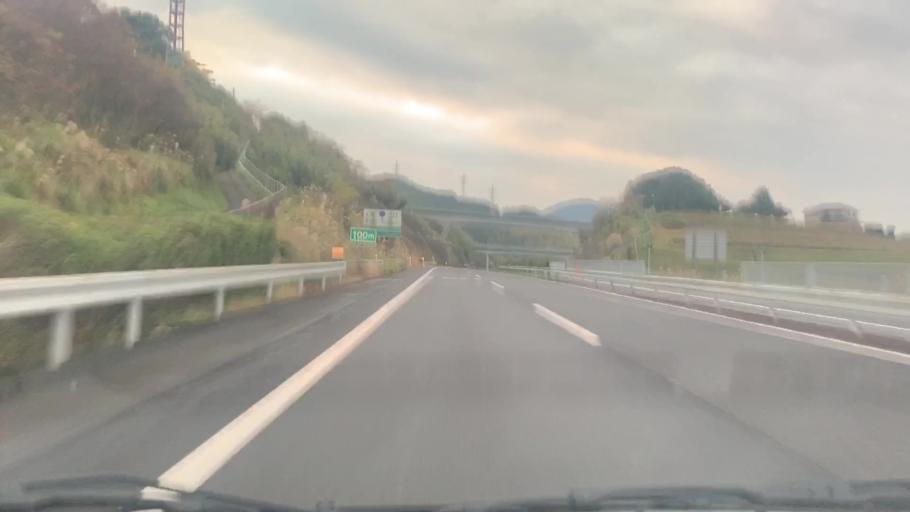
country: JP
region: Nagasaki
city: Omura
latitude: 33.0107
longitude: 129.9521
